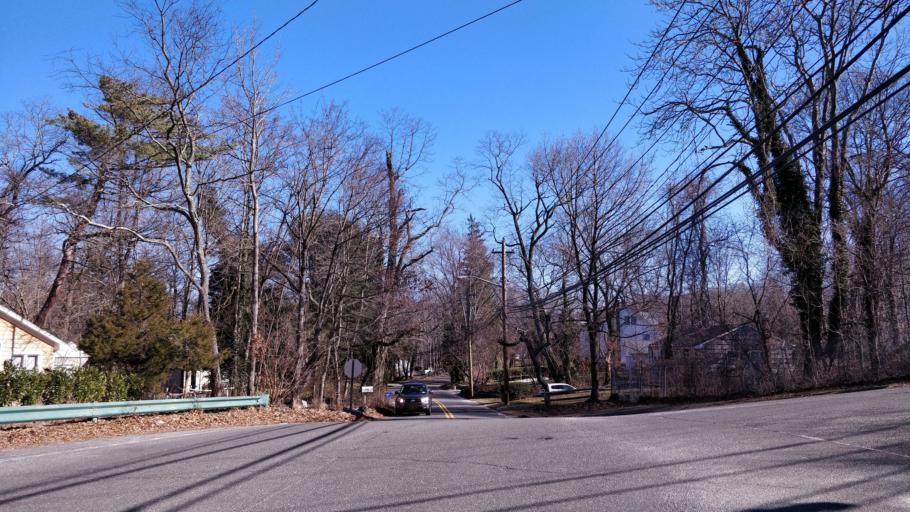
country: US
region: New York
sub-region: Suffolk County
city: Port Jefferson
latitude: 40.9476
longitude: -73.0559
